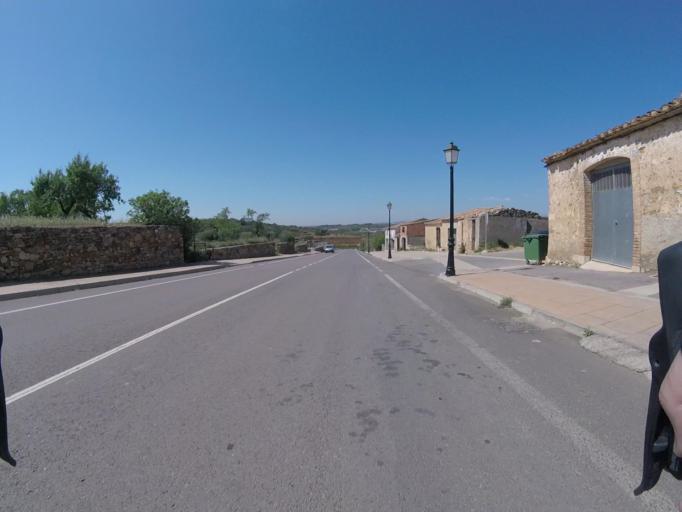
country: ES
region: Valencia
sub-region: Provincia de Castello
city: Benlloch
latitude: 40.2300
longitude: 0.0702
